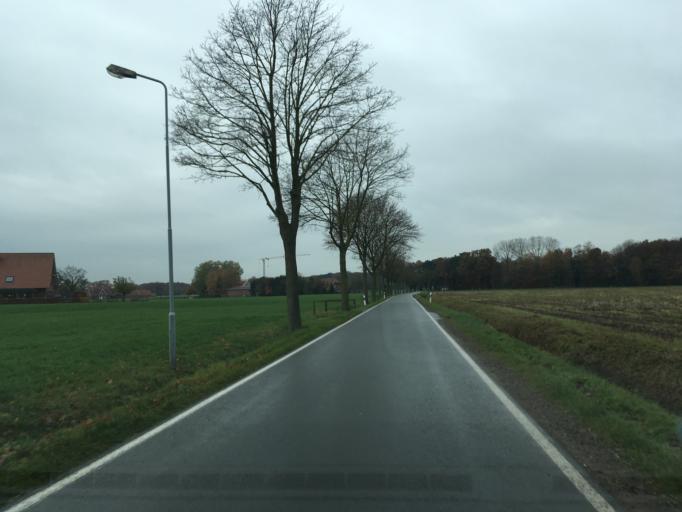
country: DE
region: North Rhine-Westphalia
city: Stadtlohn
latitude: 52.0095
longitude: 6.9463
